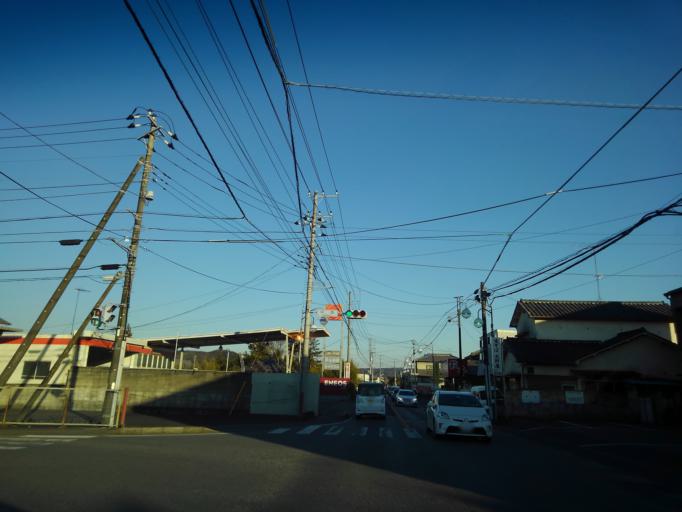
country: JP
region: Chiba
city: Kimitsu
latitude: 35.3055
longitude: 139.9587
